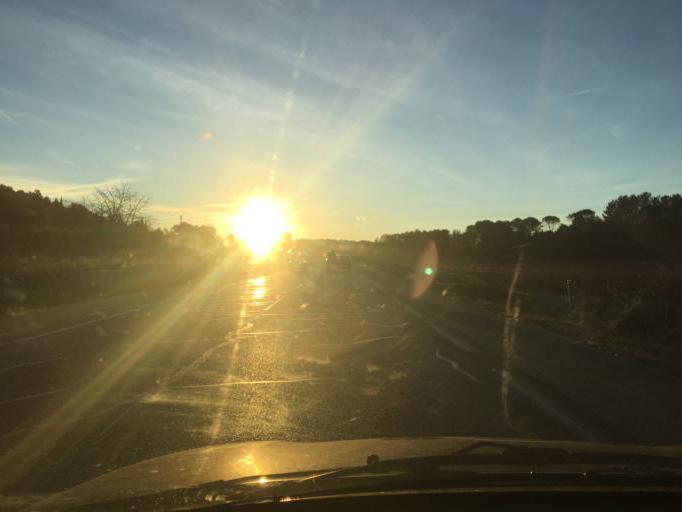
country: FR
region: Provence-Alpes-Cote d'Azur
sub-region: Departement du Var
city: Lorgues
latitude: 43.4694
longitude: 6.3833
